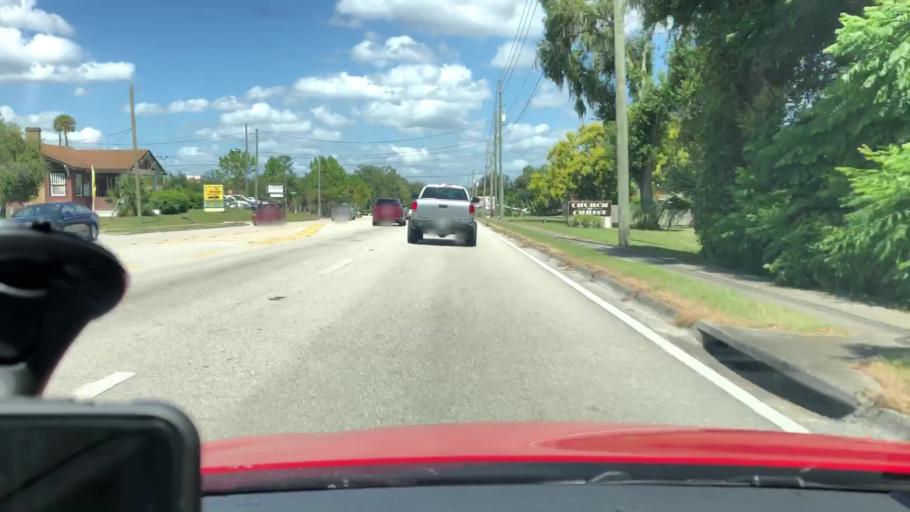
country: US
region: Florida
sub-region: Volusia County
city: West DeLand
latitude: 29.0216
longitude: -81.3239
